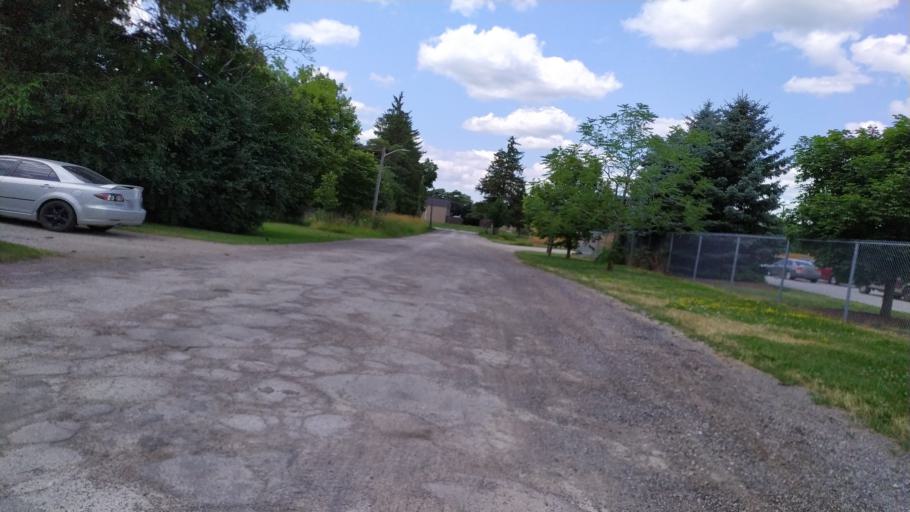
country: CA
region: Ontario
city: Stratford
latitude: 43.3595
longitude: -80.9987
